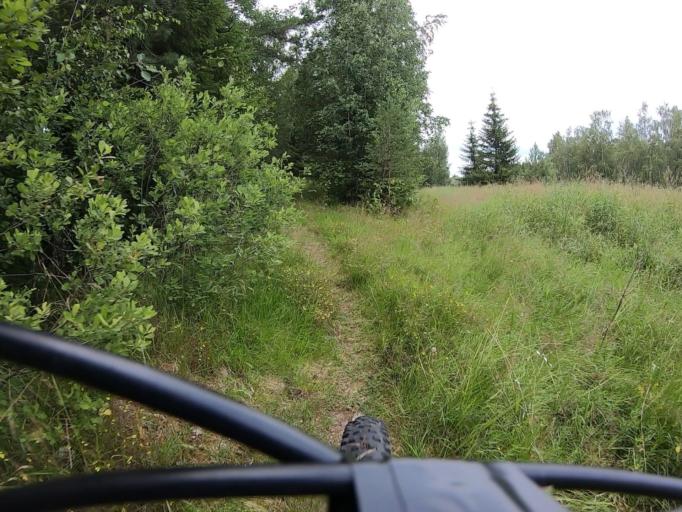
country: FI
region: Varsinais-Suomi
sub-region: Vakka-Suomi
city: Uusikaupunki
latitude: 60.8335
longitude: 21.4058
